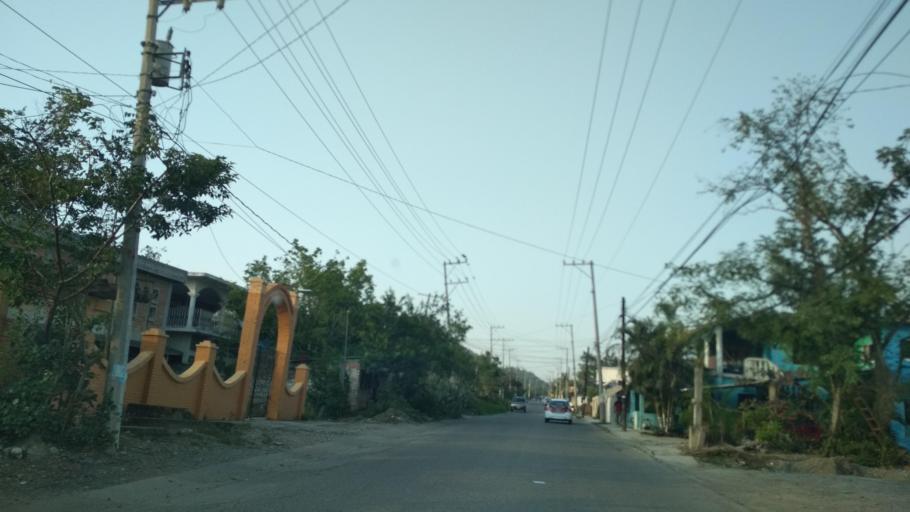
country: MM
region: Shan
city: Taunggyi
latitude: 20.4061
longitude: 97.3376
